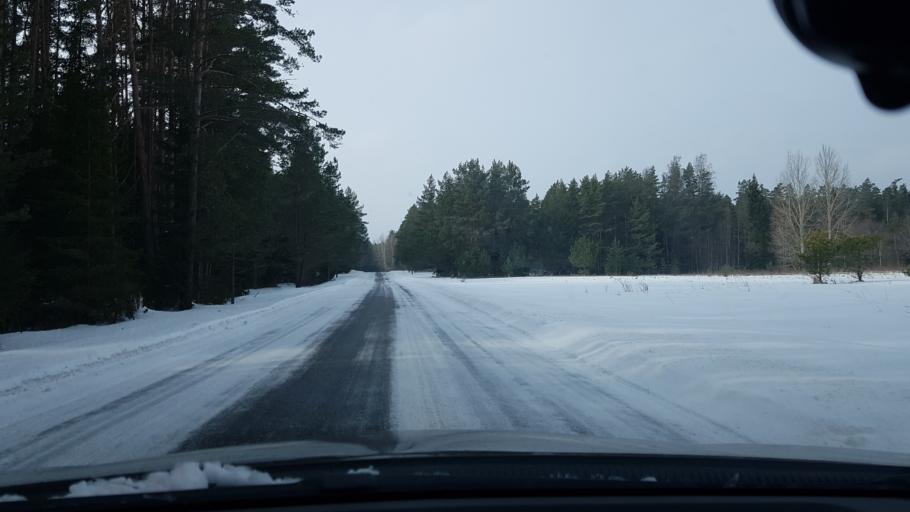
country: EE
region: Harju
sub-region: Kuusalu vald
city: Kuusalu
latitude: 59.5599
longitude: 25.5440
